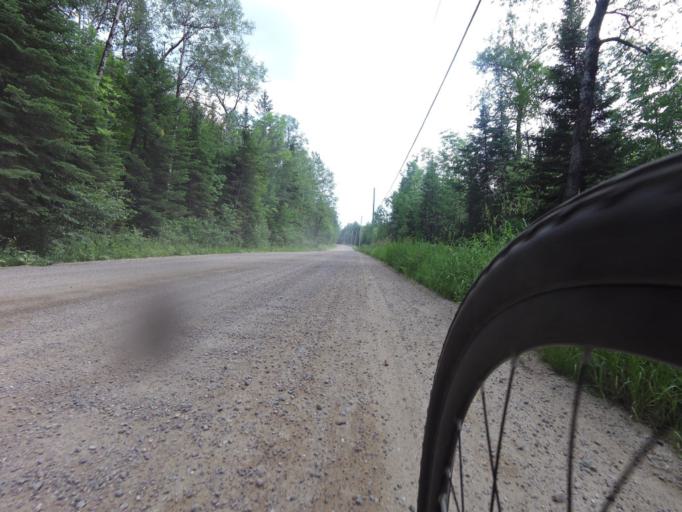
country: CA
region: Quebec
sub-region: Laurentides
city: Mont-Tremblant
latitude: 45.9254
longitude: -74.6018
